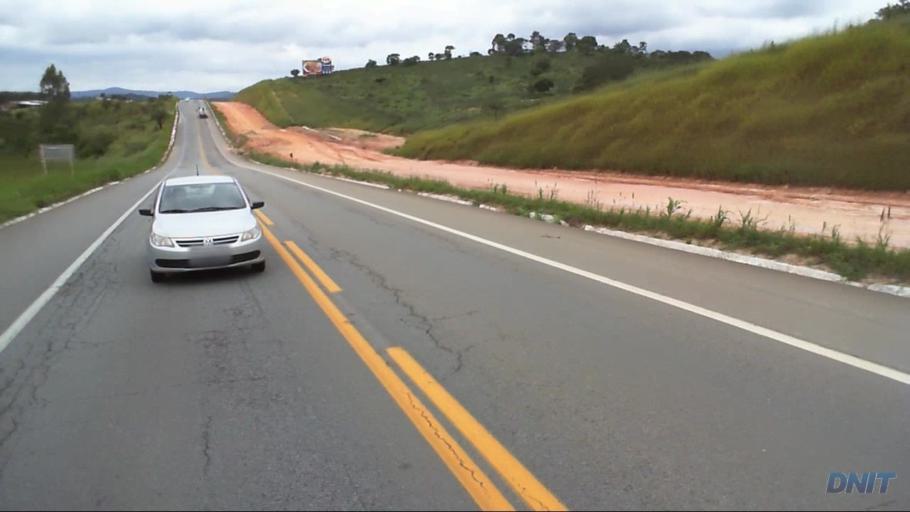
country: BR
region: Minas Gerais
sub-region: Barao De Cocais
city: Barao de Cocais
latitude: -19.7761
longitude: -43.4423
